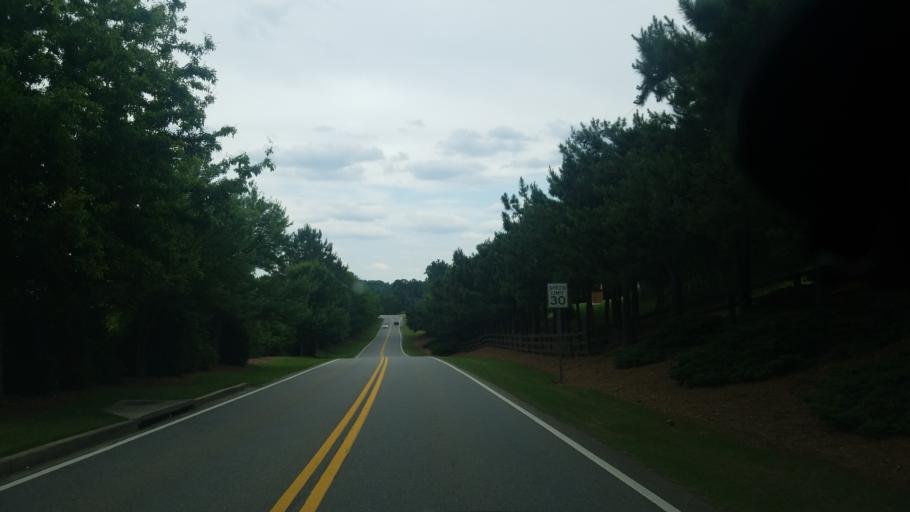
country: US
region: Georgia
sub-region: Forsyth County
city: Cumming
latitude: 34.1376
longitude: -84.1290
